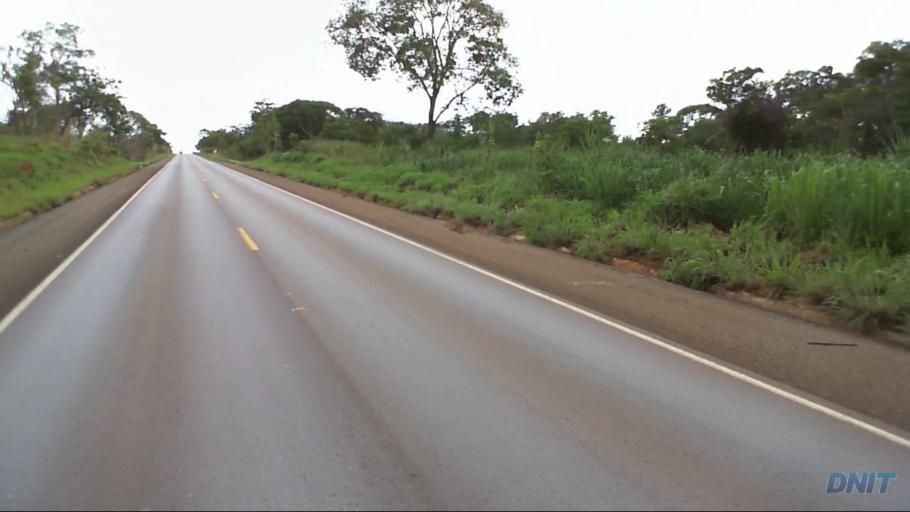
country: BR
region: Goias
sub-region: Barro Alto
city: Barro Alto
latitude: -14.8061
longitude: -49.0461
